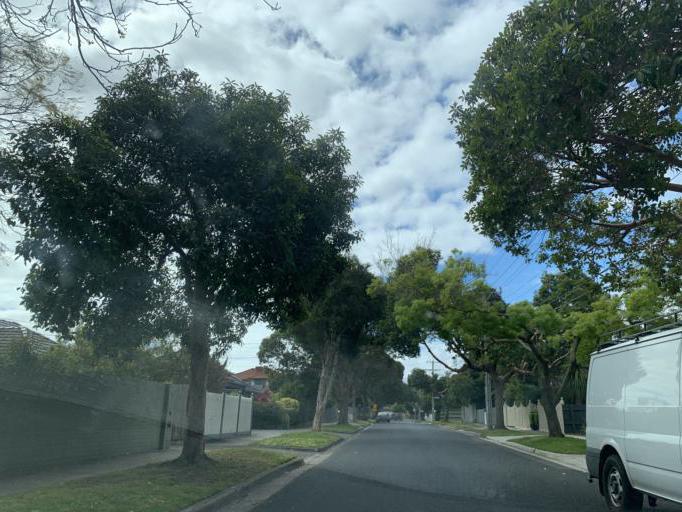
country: AU
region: Victoria
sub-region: Bayside
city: Cheltenham
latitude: -37.9733
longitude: 145.0477
